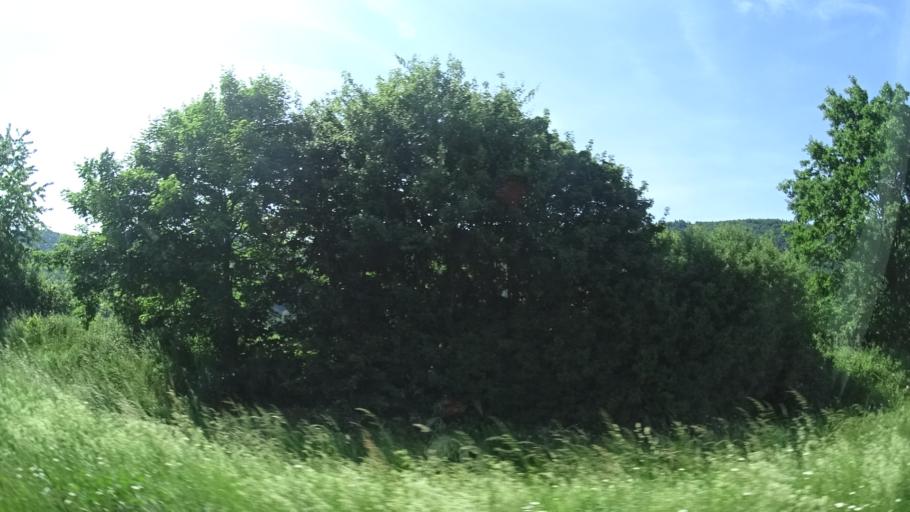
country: DE
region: Bavaria
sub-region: Regierungsbezirk Unterfranken
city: Burgstadt
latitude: 49.7294
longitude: 9.2768
